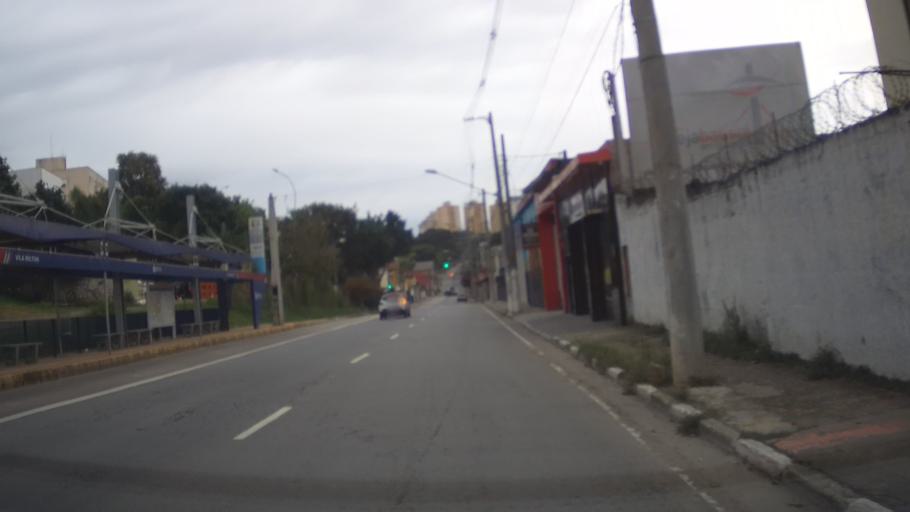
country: BR
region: Sao Paulo
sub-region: Guarulhos
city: Guarulhos
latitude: -23.4577
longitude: -46.5572
